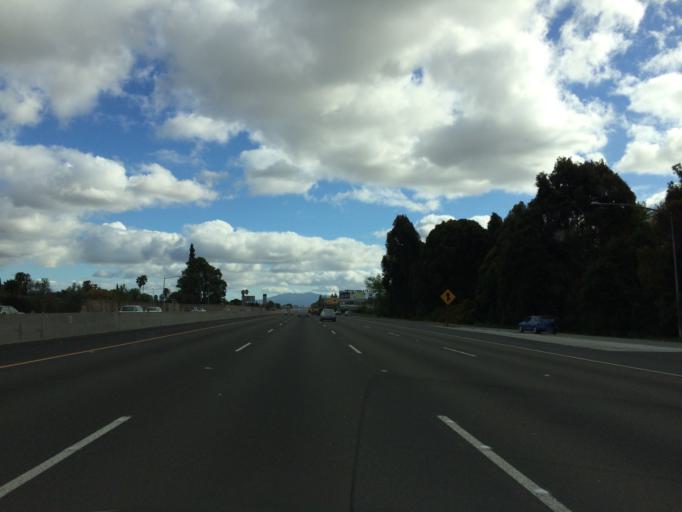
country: US
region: California
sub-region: Santa Clara County
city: Milpitas
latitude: 37.3995
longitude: -121.9086
